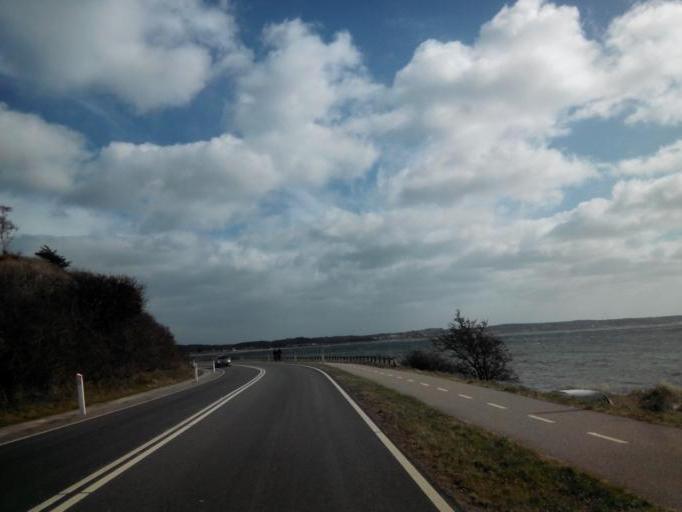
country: DK
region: Central Jutland
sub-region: Syddjurs Kommune
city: Ebeltoft
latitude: 56.2265
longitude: 10.6462
